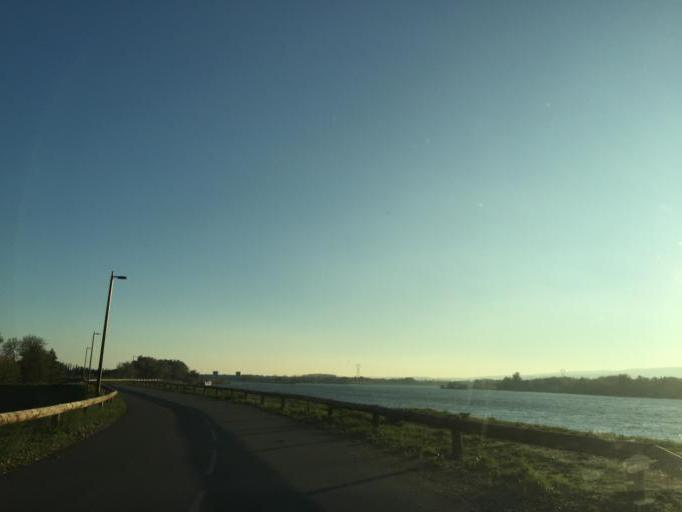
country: FR
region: Rhone-Alpes
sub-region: Departement de la Drome
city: Donzere
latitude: 44.4517
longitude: 4.7003
